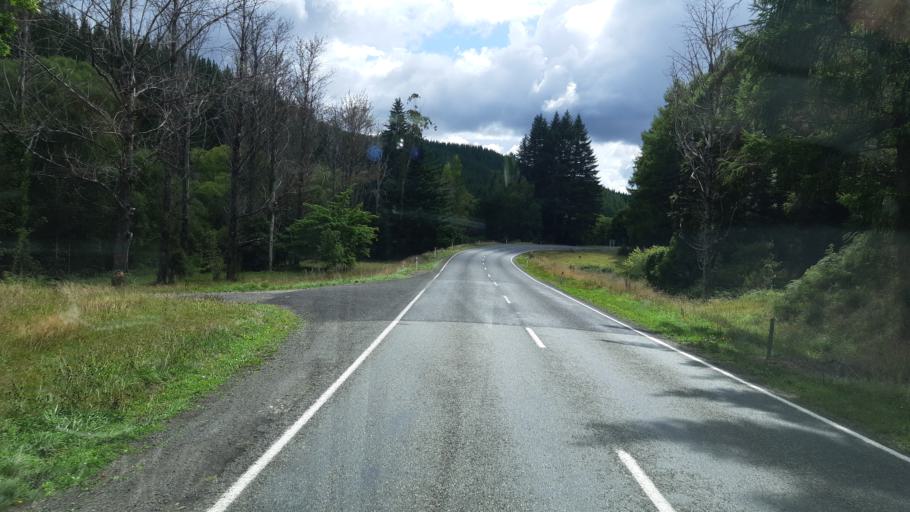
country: NZ
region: Tasman
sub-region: Tasman District
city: Wakefield
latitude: -41.6041
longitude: 172.7589
